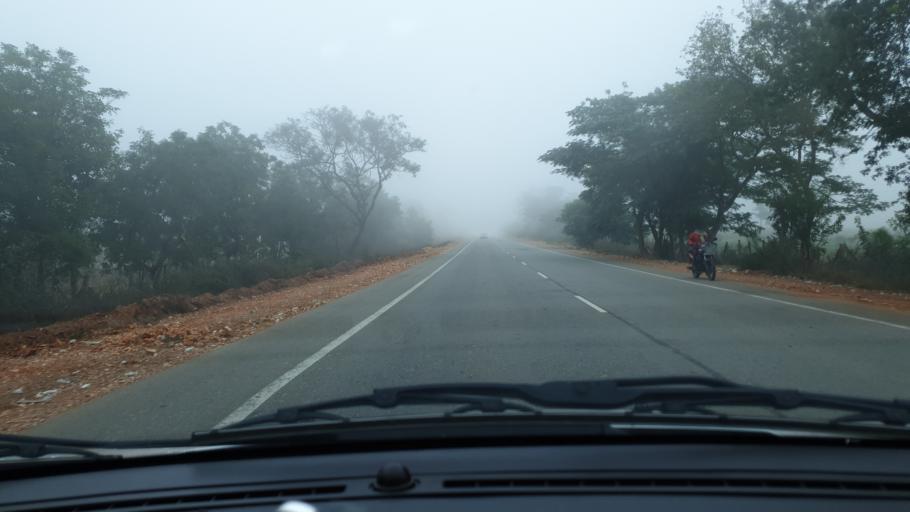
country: IN
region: Telangana
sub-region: Mahbubnagar
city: Nagar Karnul
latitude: 16.6393
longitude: 78.5951
